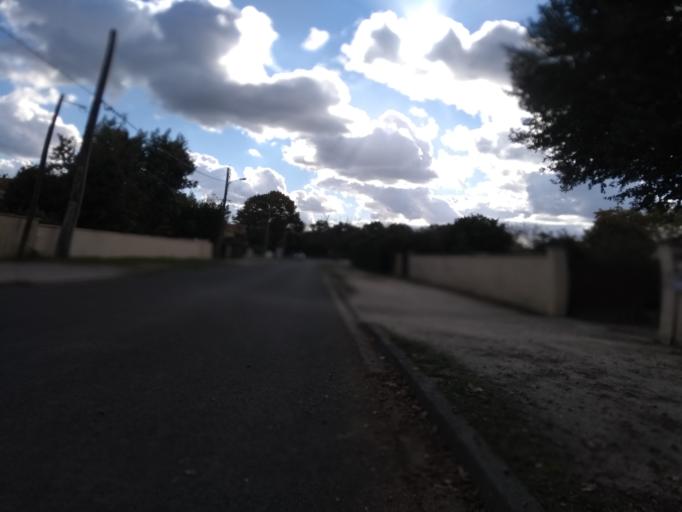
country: FR
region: Aquitaine
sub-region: Departement de la Gironde
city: Cestas
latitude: 44.7339
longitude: -0.6664
